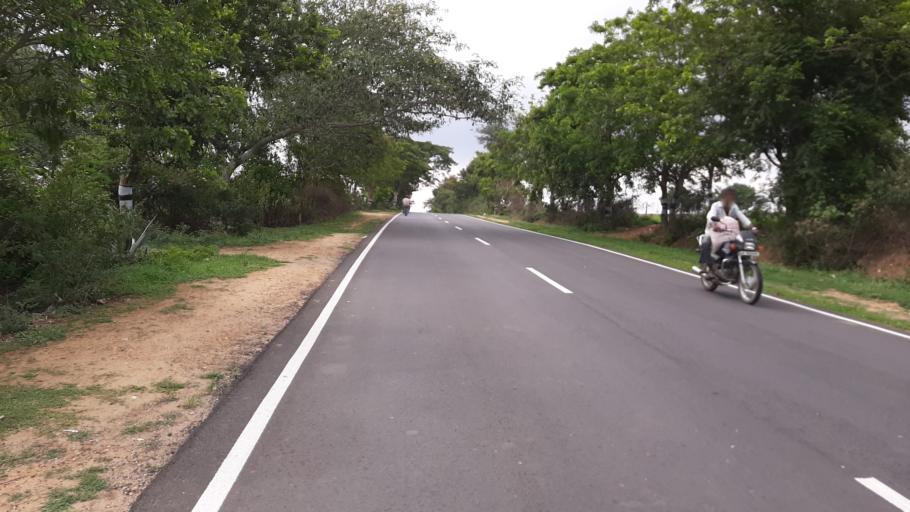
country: IN
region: Tamil Nadu
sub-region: Krishnagiri
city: Denkanikota
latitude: 12.5339
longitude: 77.7769
